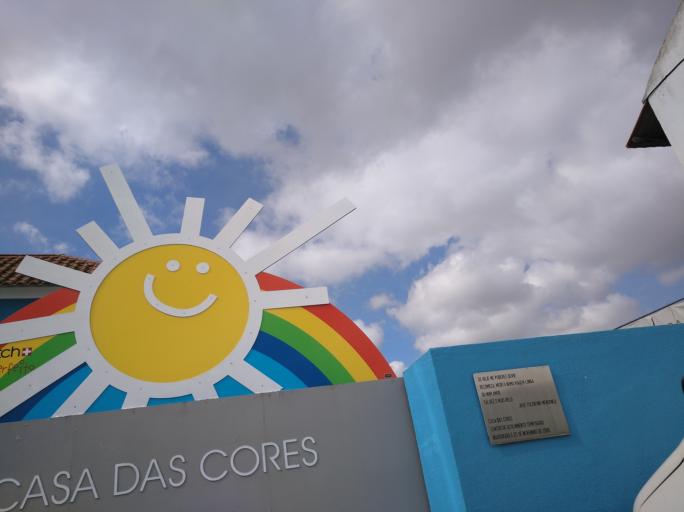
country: PT
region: Lisbon
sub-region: Lisbon
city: Lisbon
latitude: 38.7457
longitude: -9.1250
